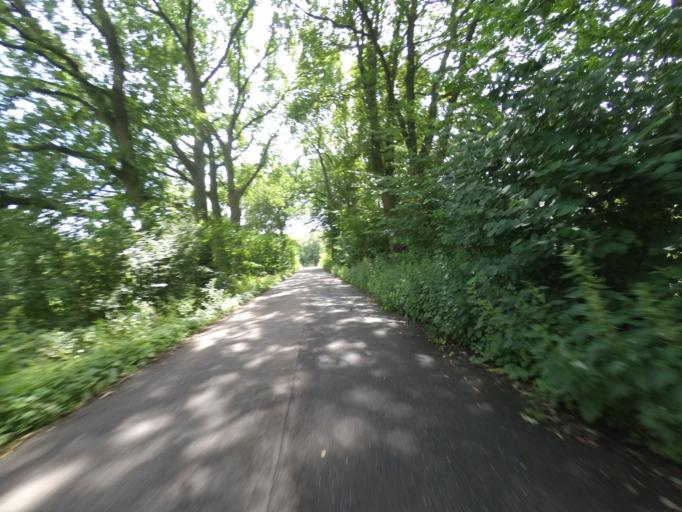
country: DE
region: Schleswig-Holstein
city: Barsbuettel
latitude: 53.5664
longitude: 10.1429
